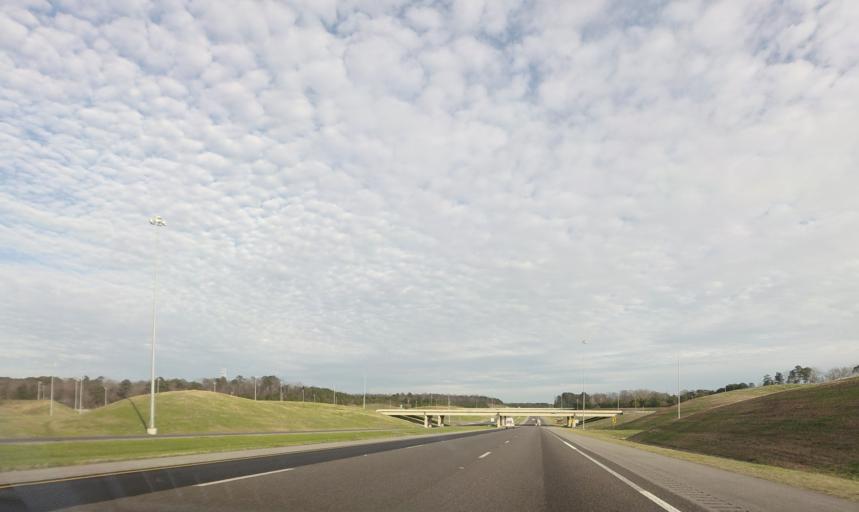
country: US
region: Alabama
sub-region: Jefferson County
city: Graysville
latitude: 33.6455
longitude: -86.9796
